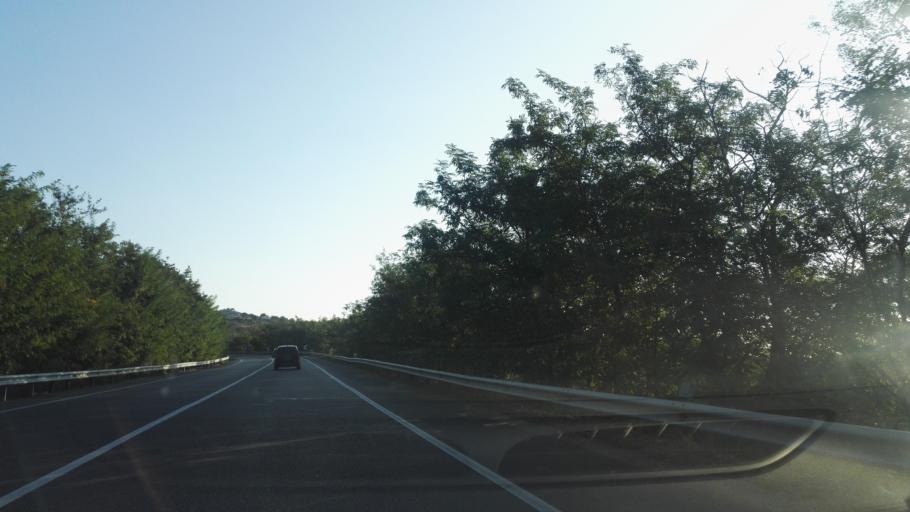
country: IT
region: Calabria
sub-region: Provincia di Catanzaro
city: Montepaone Lido
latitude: 38.7360
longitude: 16.5447
